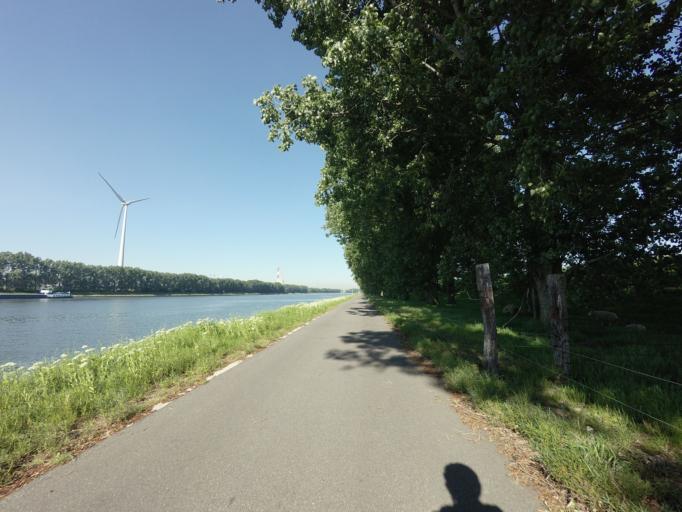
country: NL
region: North Brabant
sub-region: Gemeente Woensdrecht
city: Woensdrecht
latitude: 51.3743
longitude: 4.2957
